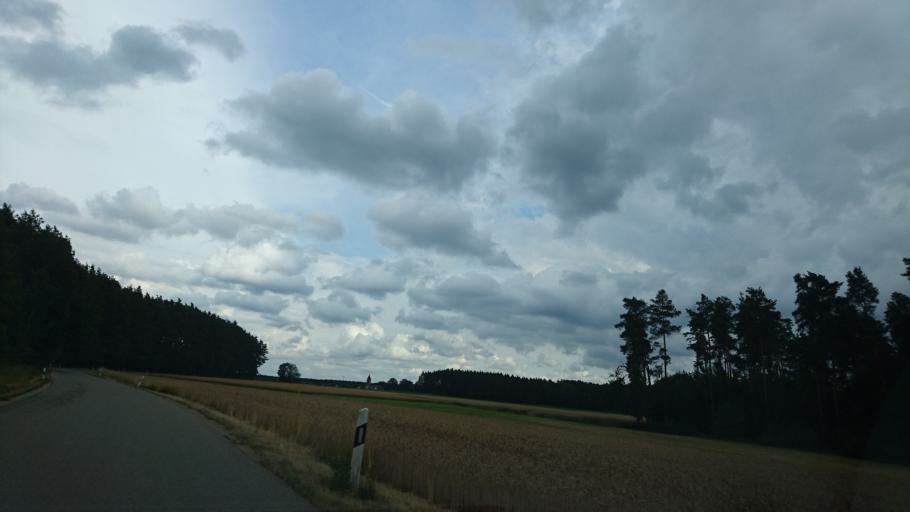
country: DE
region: Bavaria
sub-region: Regierungsbezirk Mittelfranken
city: Roth
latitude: 49.1977
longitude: 11.0961
